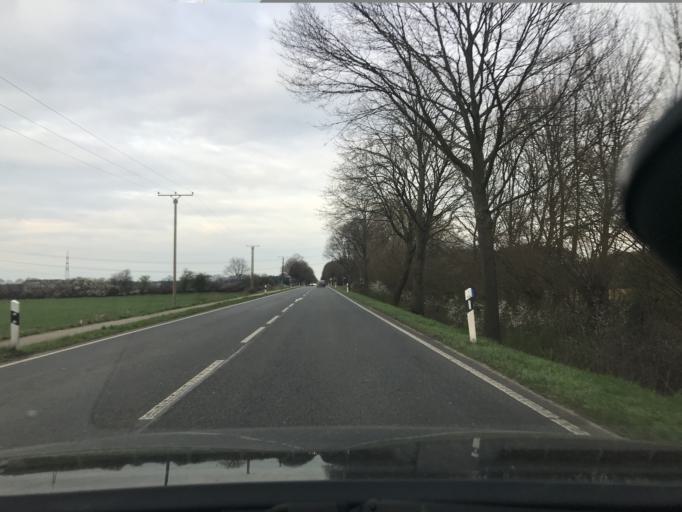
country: DE
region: North Rhine-Westphalia
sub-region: Regierungsbezirk Dusseldorf
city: Wesel
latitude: 51.6862
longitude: 6.6543
